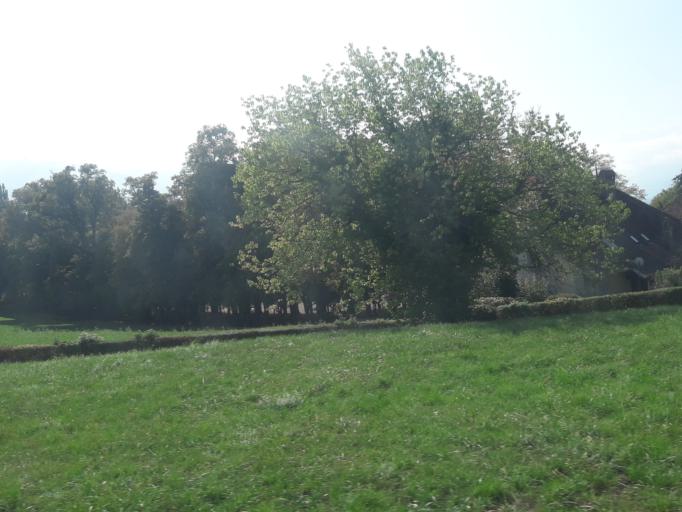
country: CH
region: Vaud
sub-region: Riviera-Pays-d'Enhaut District
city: La Tour-de-Peilz
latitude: 46.4689
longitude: 6.8658
